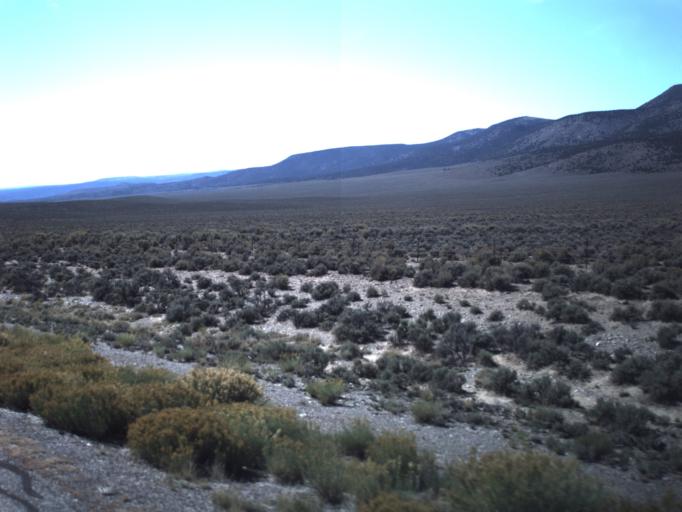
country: US
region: Utah
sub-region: Piute County
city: Junction
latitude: 38.2549
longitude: -111.9864
